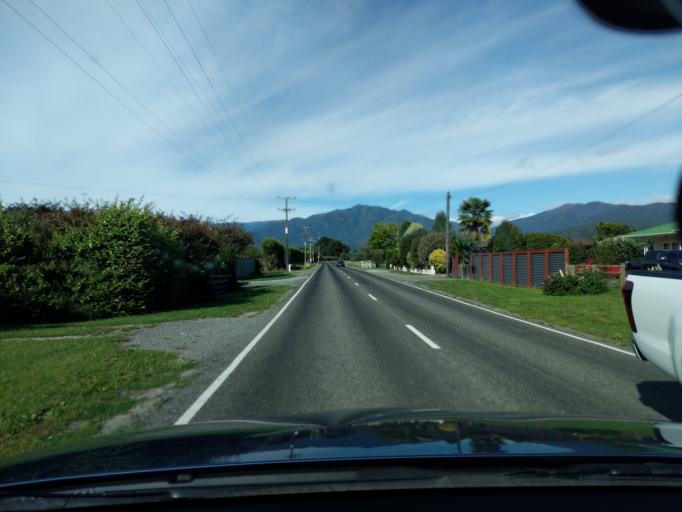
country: NZ
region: Tasman
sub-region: Tasman District
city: Takaka
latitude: -40.8556
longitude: 172.8244
